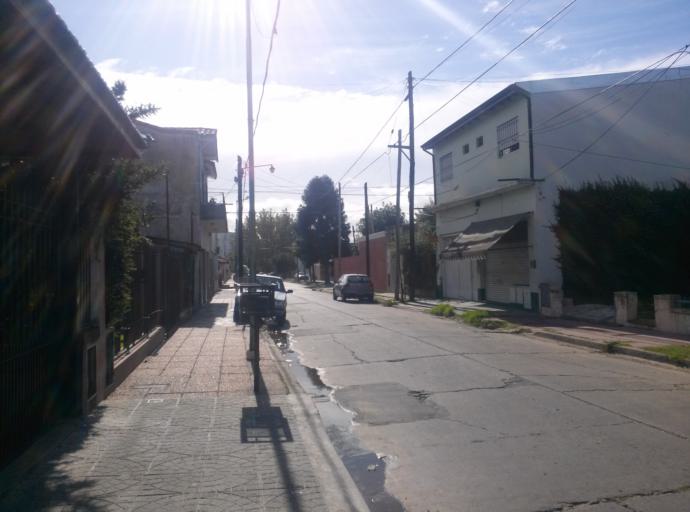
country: AR
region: Buenos Aires
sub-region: Partido de Lomas de Zamora
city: Lomas de Zamora
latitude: -34.7792
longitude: -58.4103
